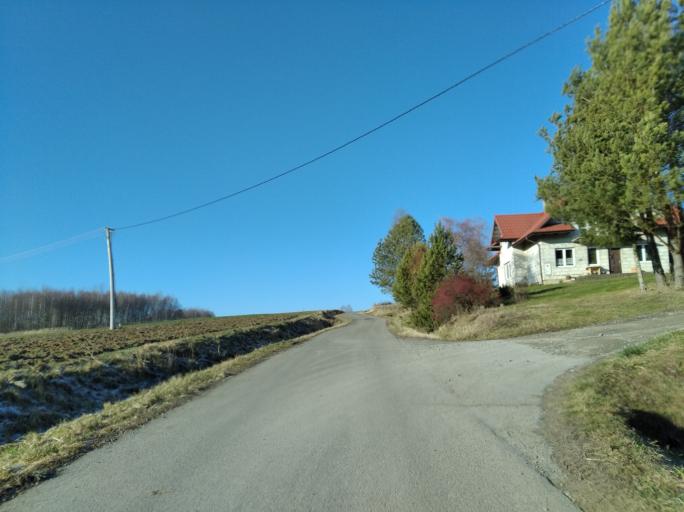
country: PL
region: Subcarpathian Voivodeship
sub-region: Powiat strzyzowski
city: Wysoka Strzyzowska
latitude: 49.8507
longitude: 21.7588
